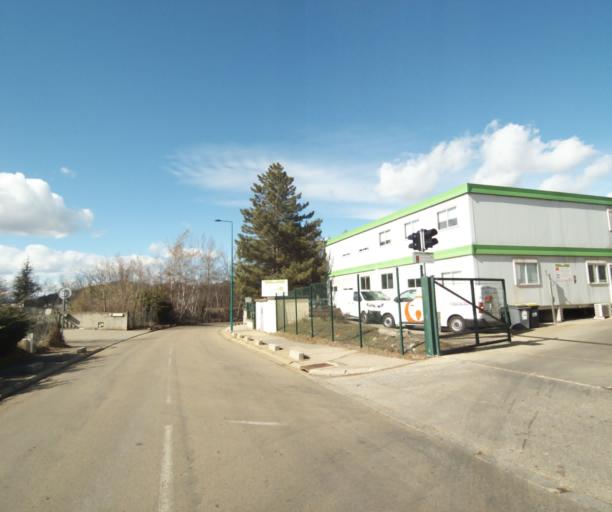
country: FR
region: Rhone-Alpes
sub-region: Departement de la Loire
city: La Talaudiere
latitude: 45.4727
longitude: 4.4317
